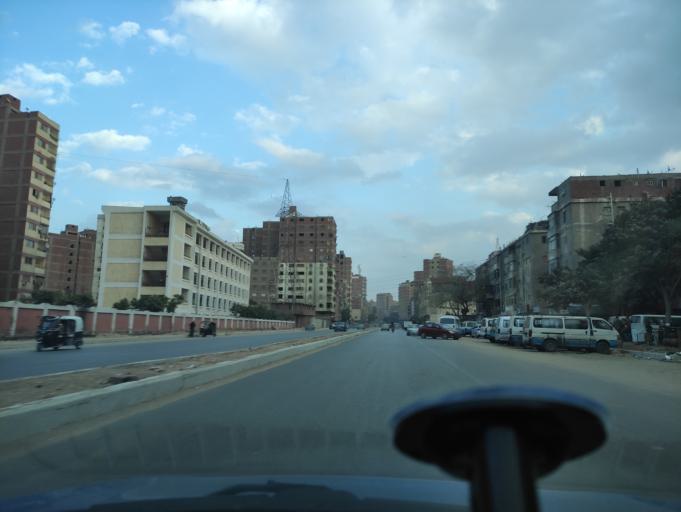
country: EG
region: Muhafazat al Qalyubiyah
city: Al Khankah
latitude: 30.1339
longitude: 31.3569
